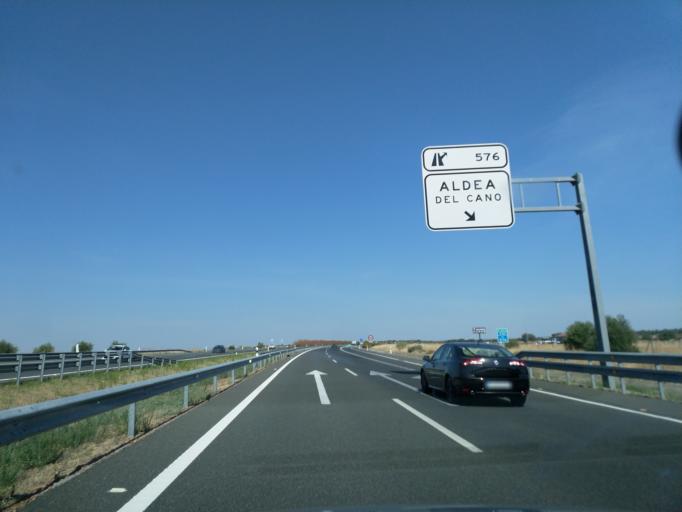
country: ES
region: Extremadura
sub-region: Provincia de Caceres
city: Aldea del Cano
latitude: 39.2847
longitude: -6.3289
